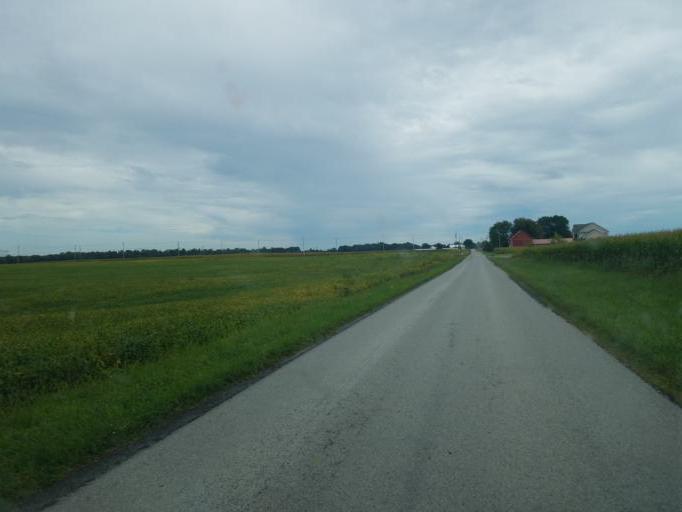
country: US
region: Ohio
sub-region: Knox County
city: Centerburg
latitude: 40.2597
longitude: -82.7221
